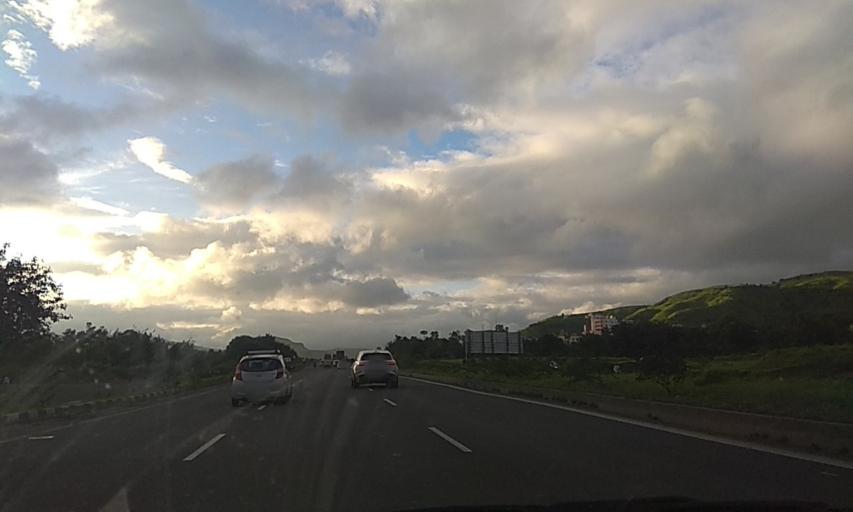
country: IN
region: Maharashtra
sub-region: Satara Division
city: Satara
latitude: 17.7350
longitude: 74.0126
